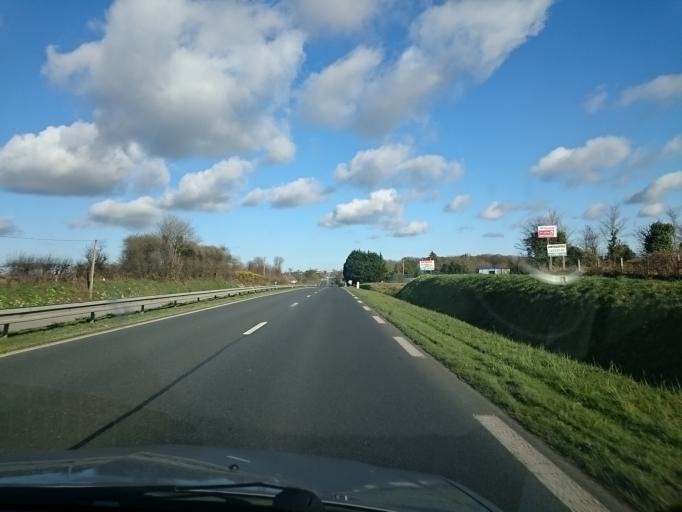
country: FR
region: Lower Normandy
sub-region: Departement de la Manche
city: Montebourg
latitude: 49.4955
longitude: -1.4239
